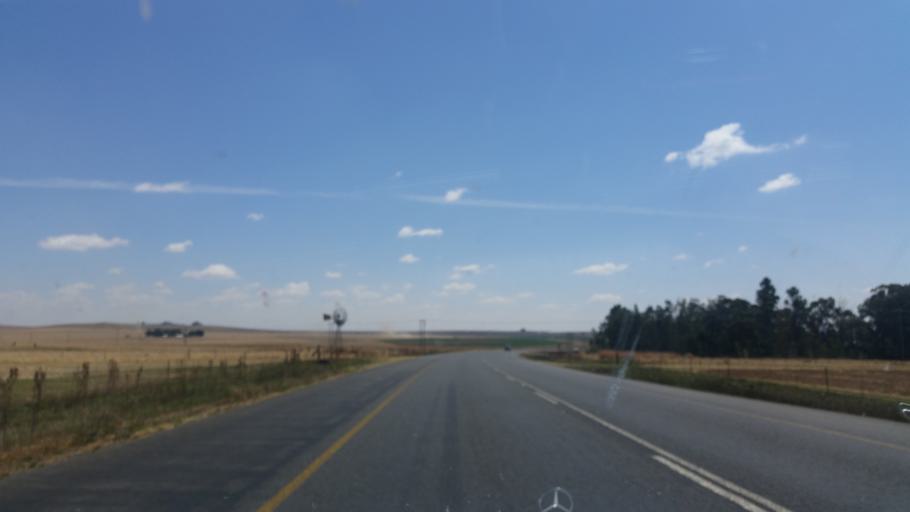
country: ZA
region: Orange Free State
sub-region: Thabo Mofutsanyana District Municipality
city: Bethlehem
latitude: -28.1069
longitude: 28.6638
